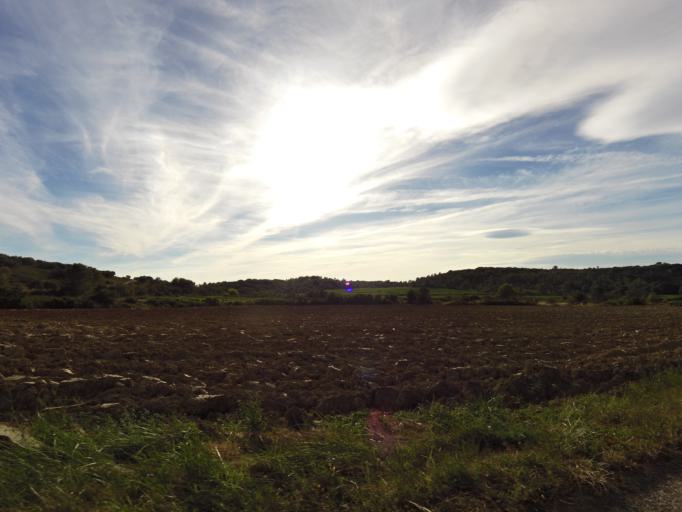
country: FR
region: Languedoc-Roussillon
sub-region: Departement du Gard
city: Congenies
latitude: 43.8067
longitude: 4.1507
